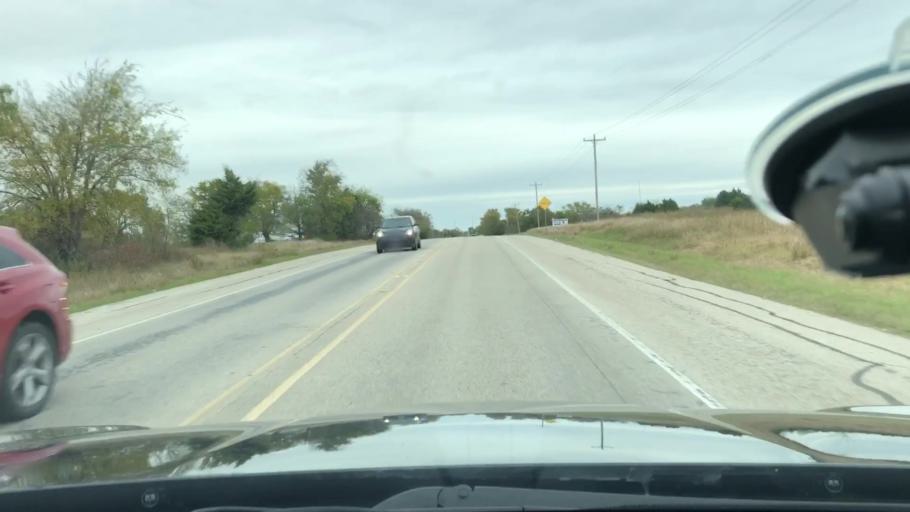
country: US
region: Texas
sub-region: Hunt County
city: Greenville
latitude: 33.0674
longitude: -96.1100
